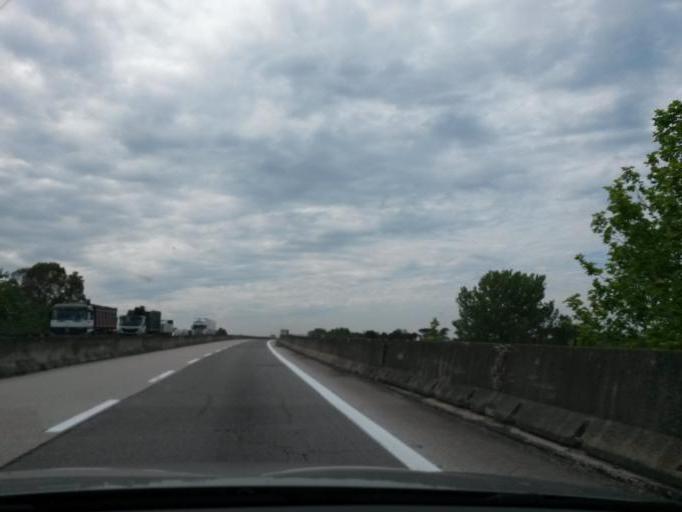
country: IT
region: Tuscany
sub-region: Provincia di Livorno
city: Donoratico
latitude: 43.1857
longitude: 10.5658
